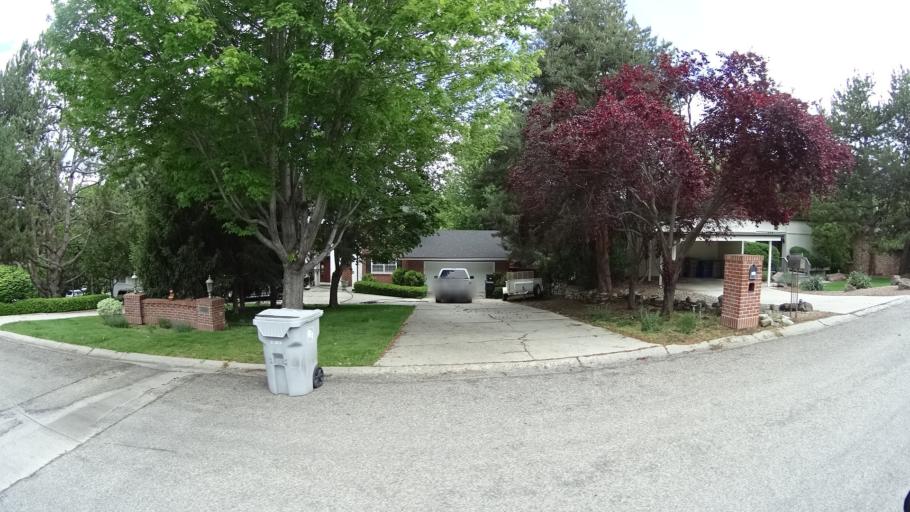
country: US
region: Idaho
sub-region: Ada County
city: Boise
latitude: 43.6473
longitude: -116.1844
